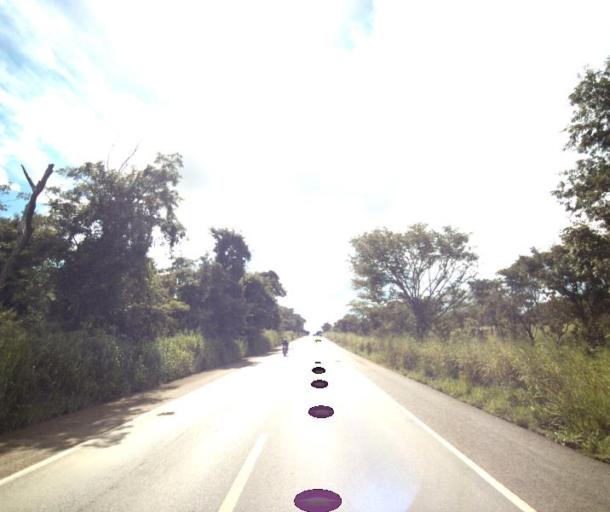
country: BR
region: Goias
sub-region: Jaragua
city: Jaragua
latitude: -15.9243
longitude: -49.2131
